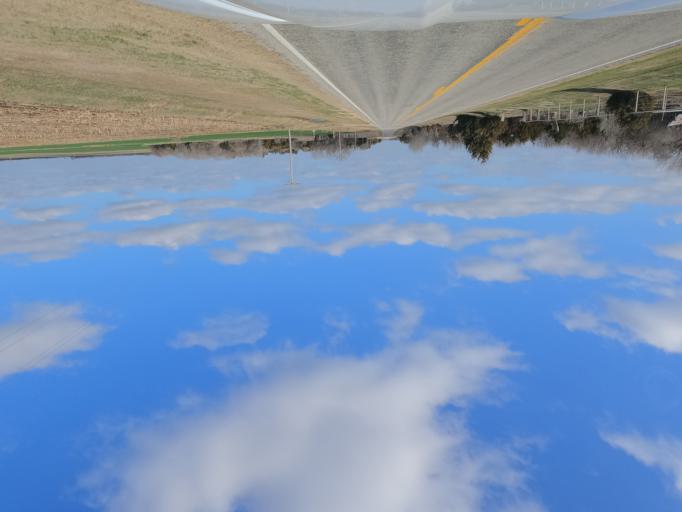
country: US
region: Kansas
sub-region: McPherson County
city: Inman
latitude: 38.2133
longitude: -97.8488
